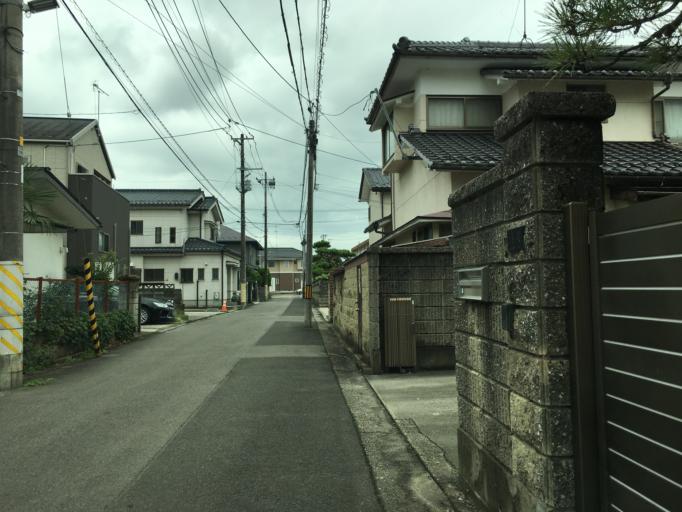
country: JP
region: Fukushima
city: Fukushima-shi
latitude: 37.7554
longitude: 140.4758
